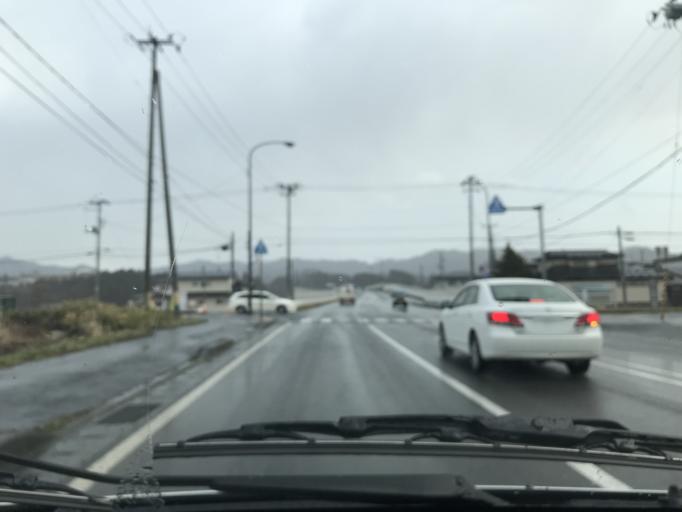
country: JP
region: Iwate
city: Kitakami
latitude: 39.2925
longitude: 141.1370
